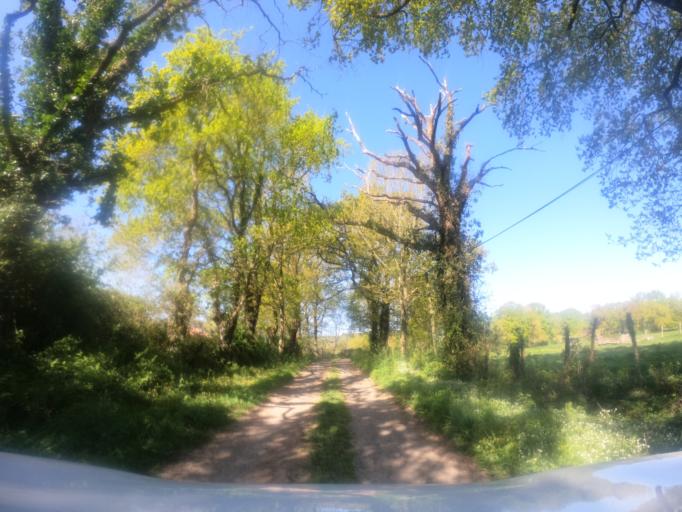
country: FR
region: Pays de la Loire
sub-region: Departement de la Vendee
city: Le Champ-Saint-Pere
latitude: 46.5140
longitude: -1.3559
